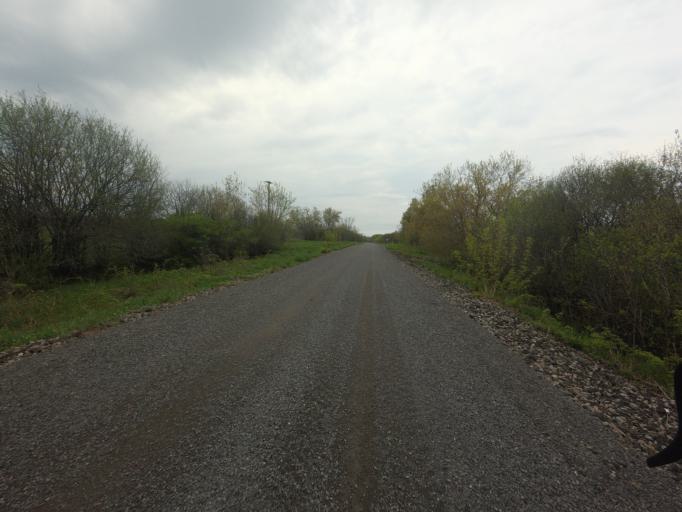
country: CA
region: Ontario
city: Carleton Place
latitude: 45.2158
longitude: -76.1822
